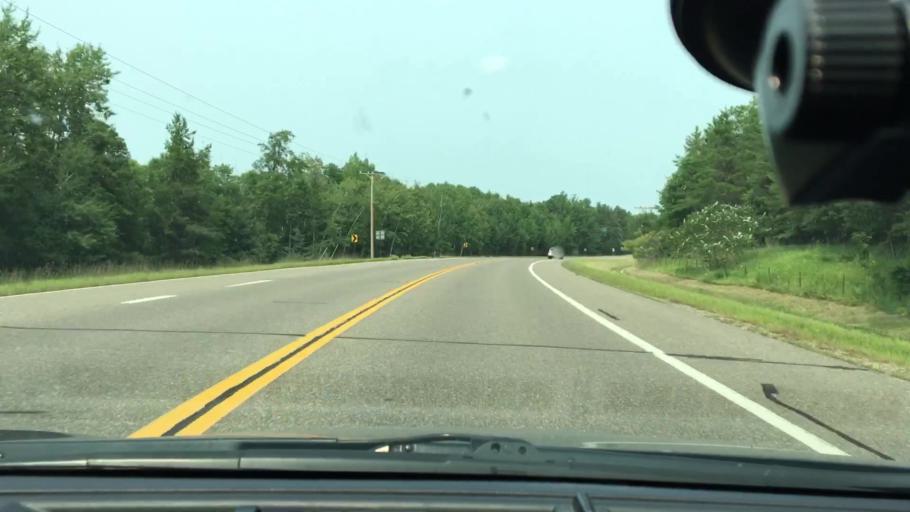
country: US
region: Minnesota
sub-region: Crow Wing County
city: Breezy Point
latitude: 46.5596
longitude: -94.1353
